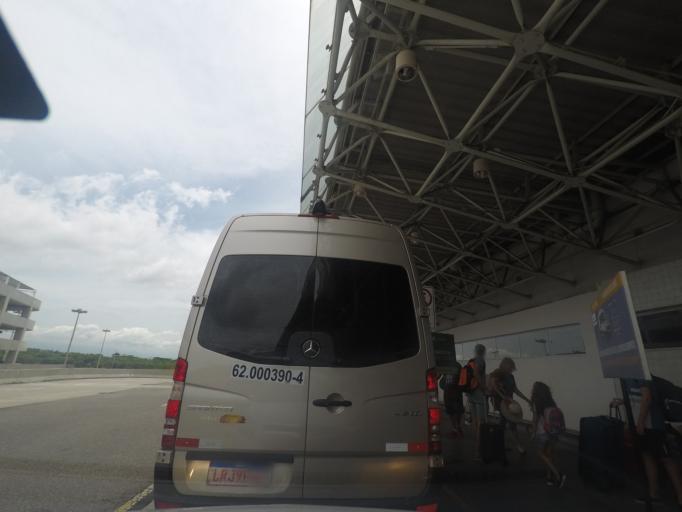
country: BR
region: Rio de Janeiro
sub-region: Duque De Caxias
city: Duque de Caxias
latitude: -22.8147
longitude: -43.2454
